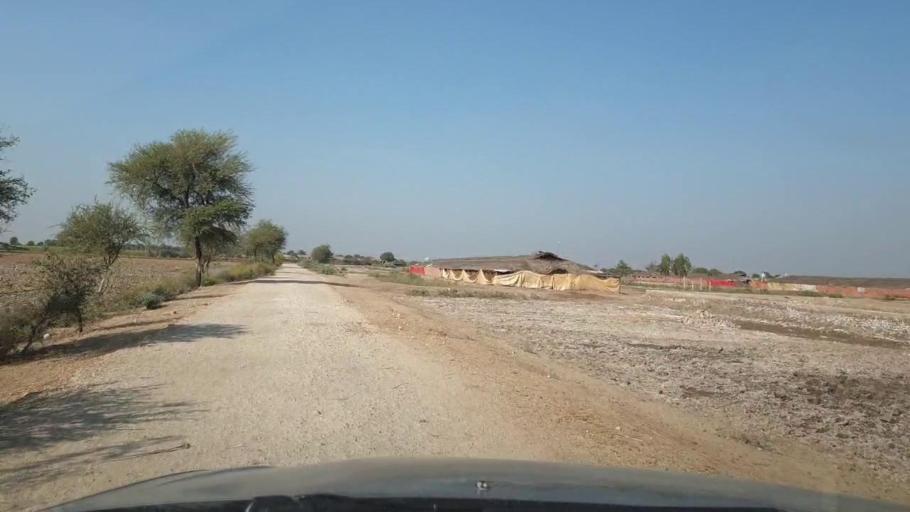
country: PK
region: Sindh
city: Tando Muhammad Khan
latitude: 25.1110
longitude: 68.5889
